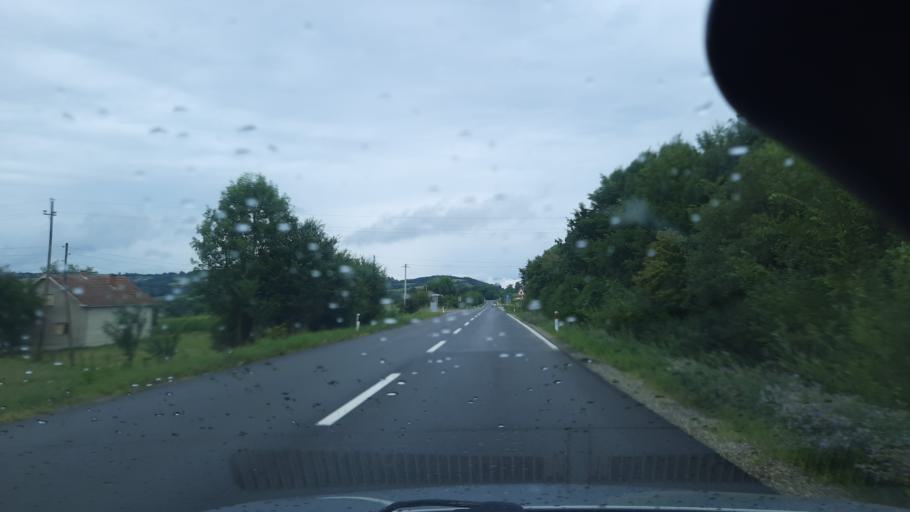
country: RS
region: Central Serbia
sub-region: Sumadijski Okrug
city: Knic
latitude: 43.8660
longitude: 20.7767
